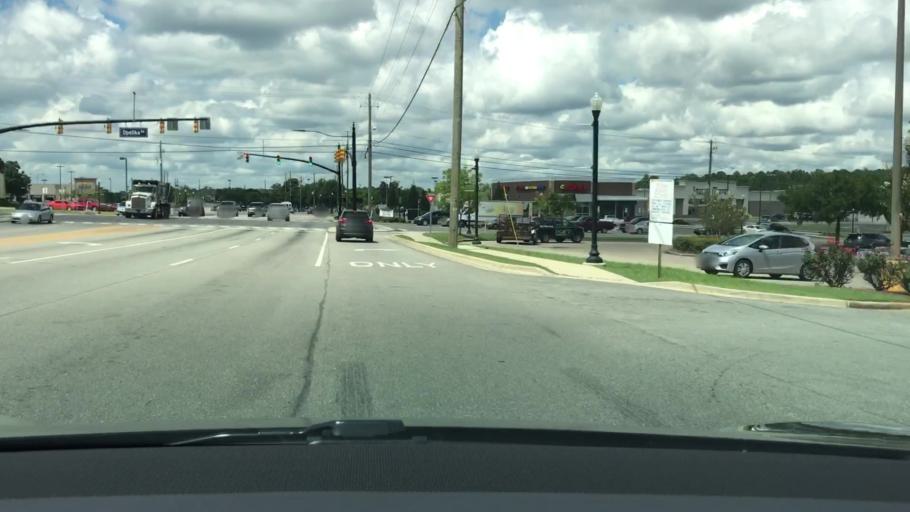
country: US
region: Alabama
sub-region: Lee County
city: Auburn
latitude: 32.6232
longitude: -85.4481
